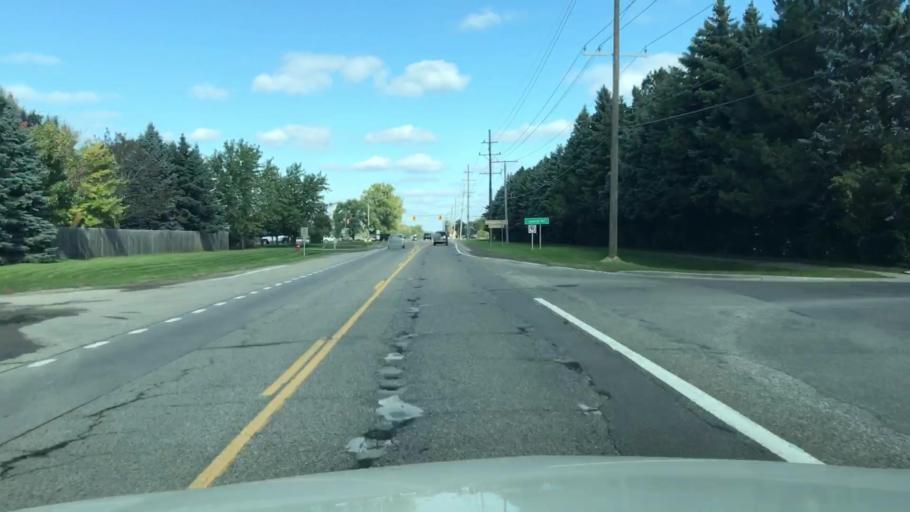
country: US
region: Michigan
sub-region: Oakland County
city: Rochester
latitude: 42.6513
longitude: -83.0927
